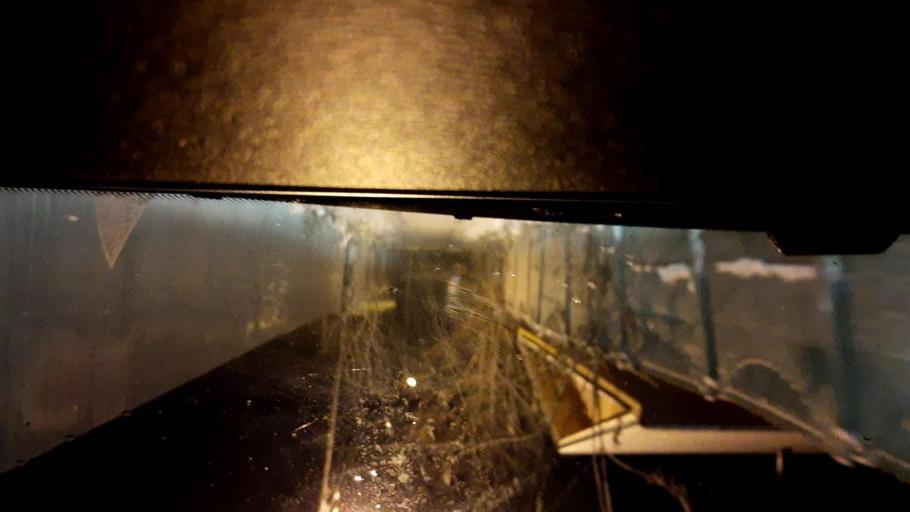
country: RU
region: Nizjnij Novgorod
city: Gorbatovka
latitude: 56.3794
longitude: 43.8229
